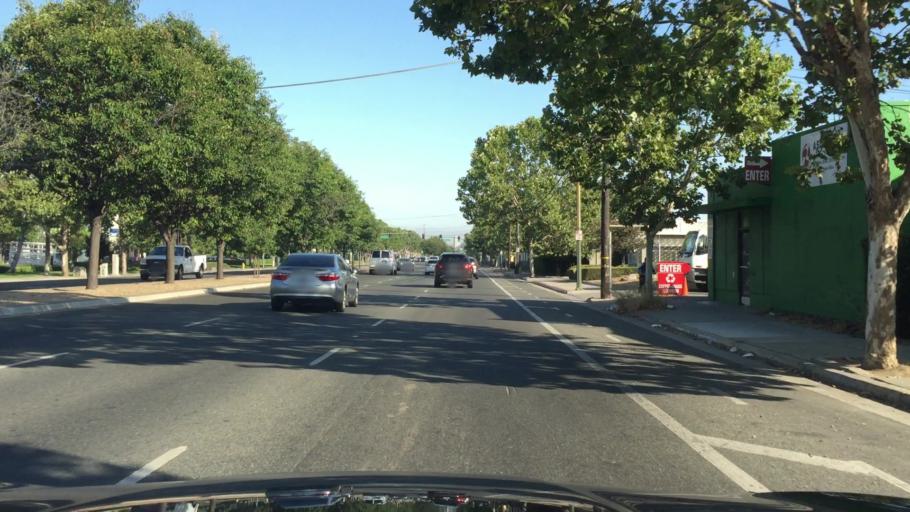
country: US
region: California
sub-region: Santa Clara County
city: Seven Trees
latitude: 37.3070
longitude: -121.8643
